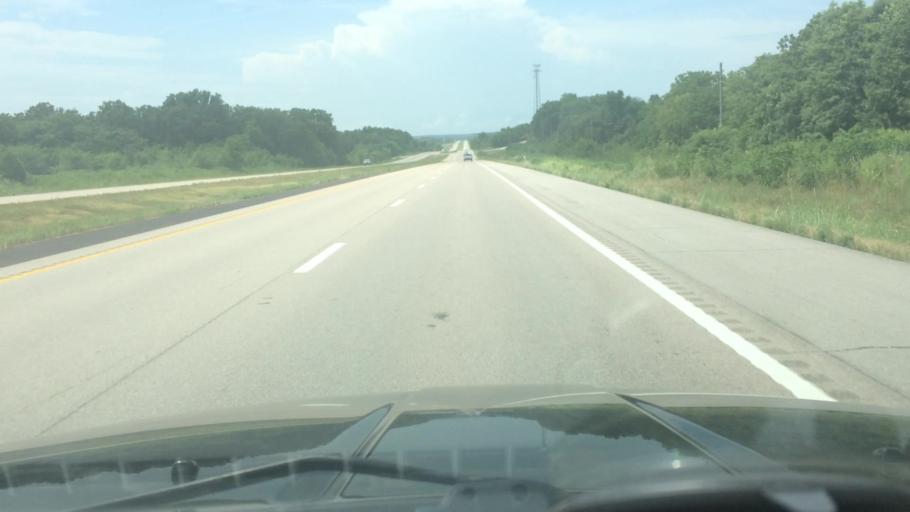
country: US
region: Missouri
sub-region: Polk County
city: Humansville
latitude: 37.7764
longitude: -93.5709
